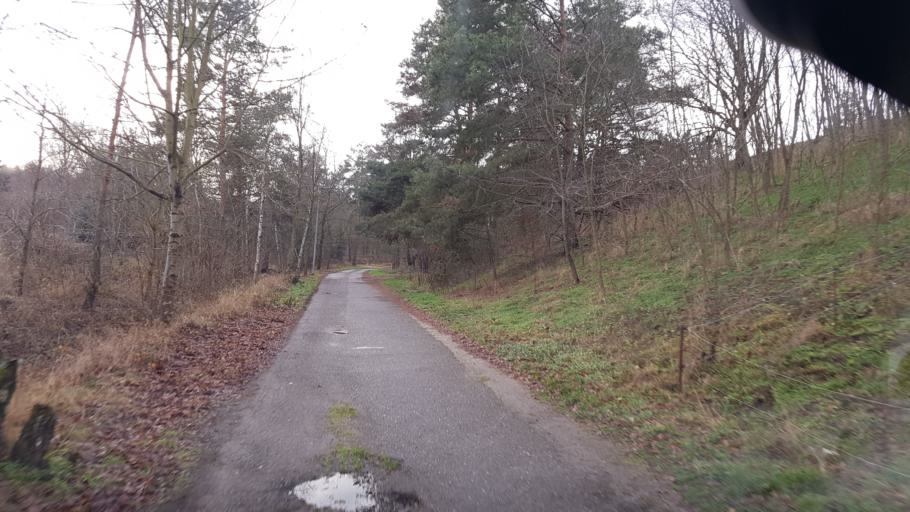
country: DE
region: Brandenburg
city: Altdobern
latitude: 51.6518
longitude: 14.0117
